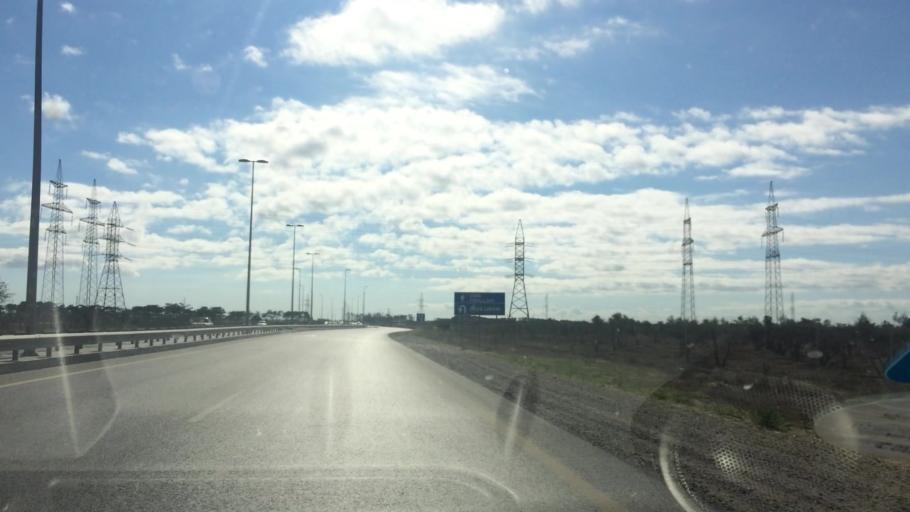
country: AZ
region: Baki
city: Qala
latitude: 40.4383
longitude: 50.1831
